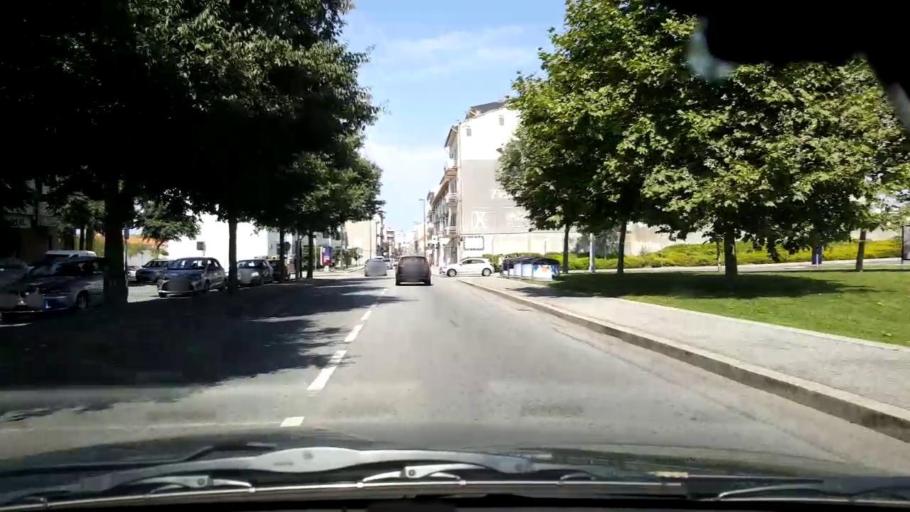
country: PT
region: Porto
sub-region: Povoa de Varzim
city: Povoa de Varzim
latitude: 41.3731
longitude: -8.7550
